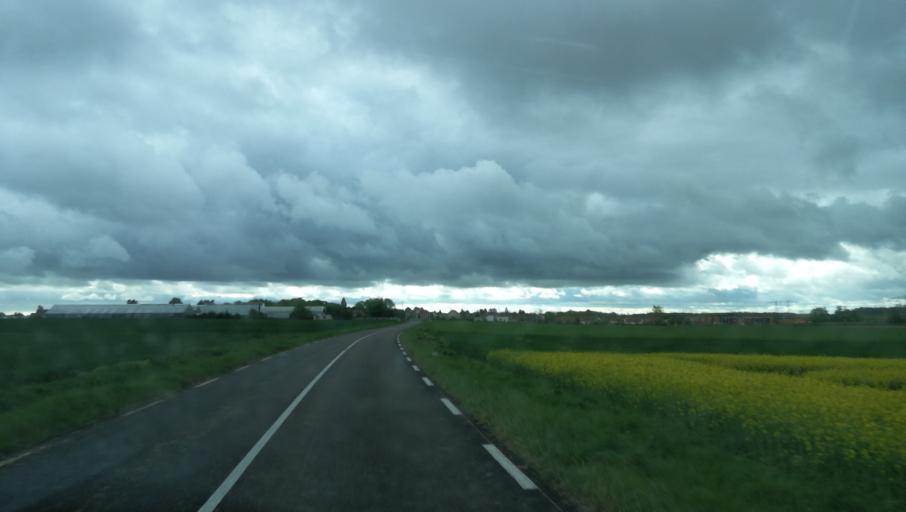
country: FR
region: Ile-de-France
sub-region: Departement de l'Essonne
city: Gometz-la-Ville
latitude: 48.6747
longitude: 2.1095
